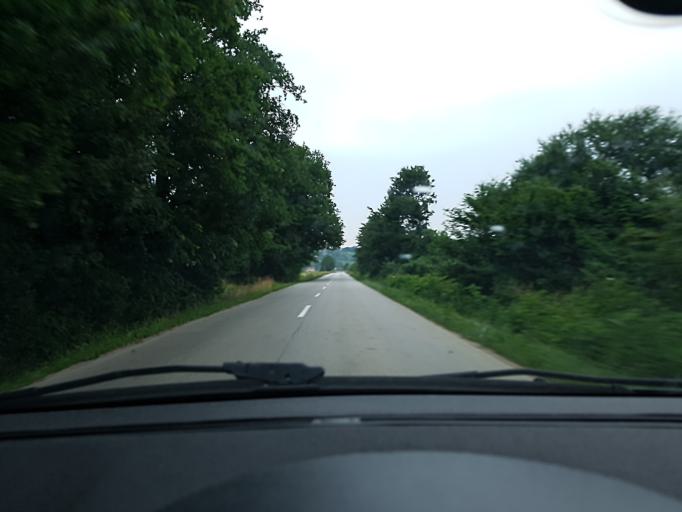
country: HR
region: Zagrebacka
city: Pojatno
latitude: 45.9424
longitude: 15.8121
